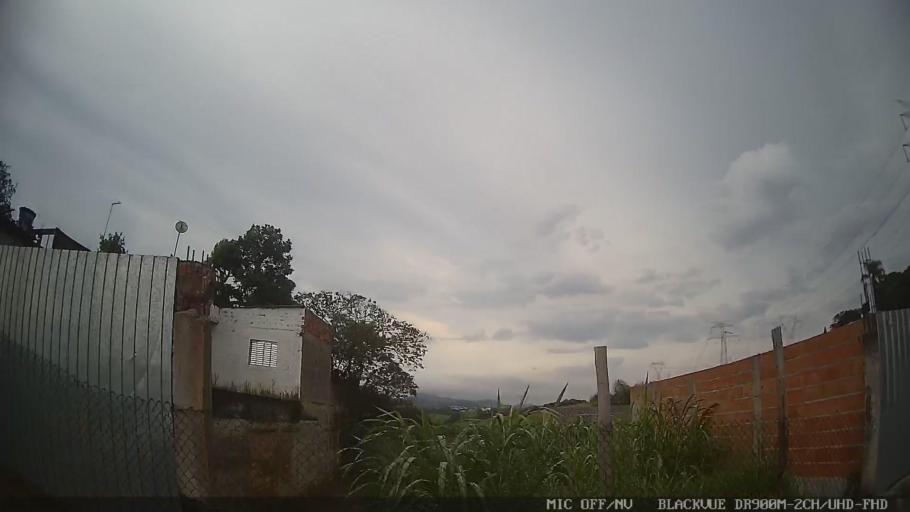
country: BR
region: Sao Paulo
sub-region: Aruja
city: Aruja
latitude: -23.4459
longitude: -46.2803
